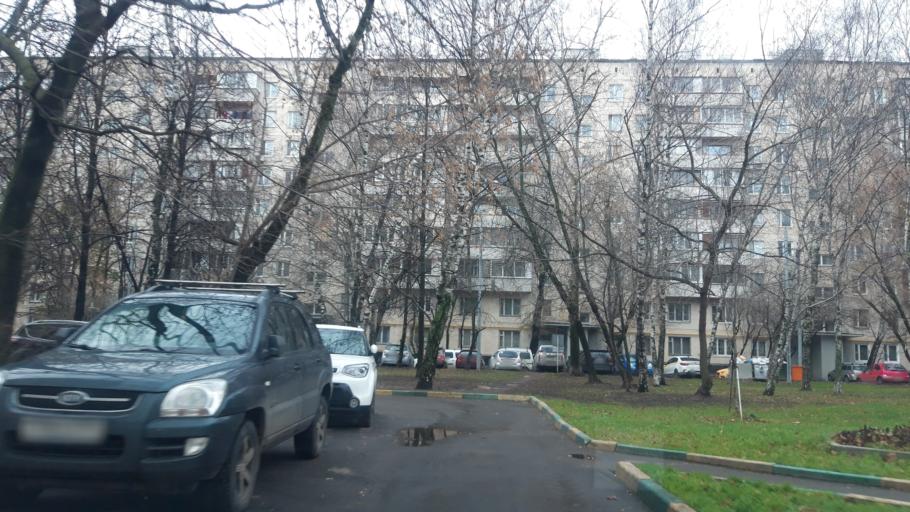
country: RU
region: Moscow
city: Likhobory
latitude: 55.8315
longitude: 37.5706
